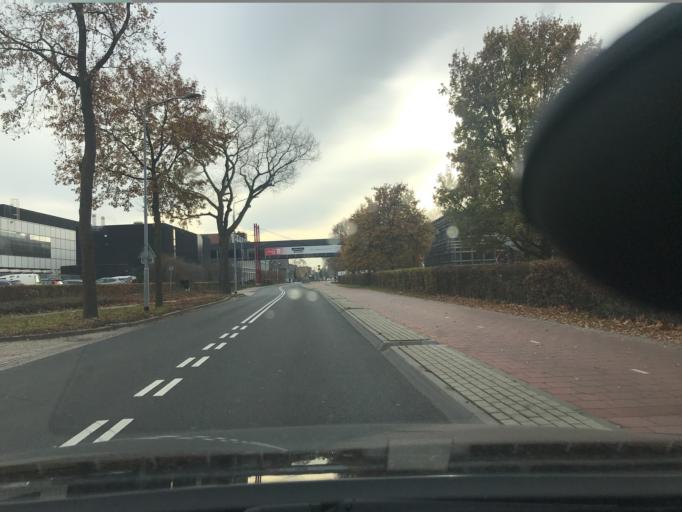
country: NL
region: Limburg
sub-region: Gemeente Venlo
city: Venlo
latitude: 51.3876
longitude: 6.1680
